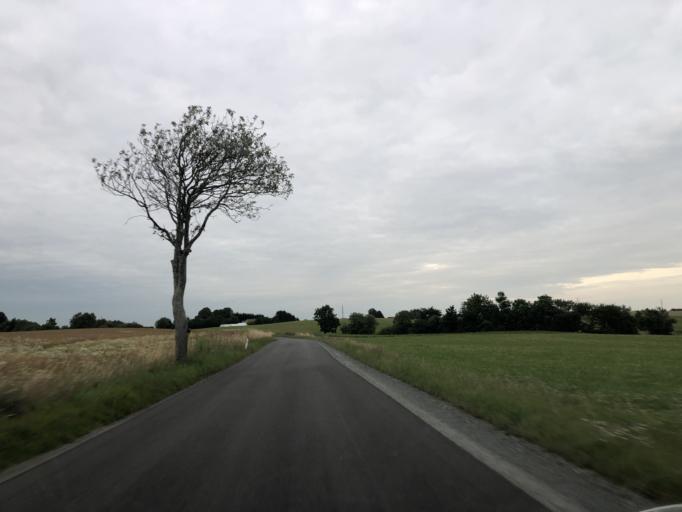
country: DK
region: South Denmark
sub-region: Vejle Kommune
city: Jelling
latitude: 55.7173
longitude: 9.3925
